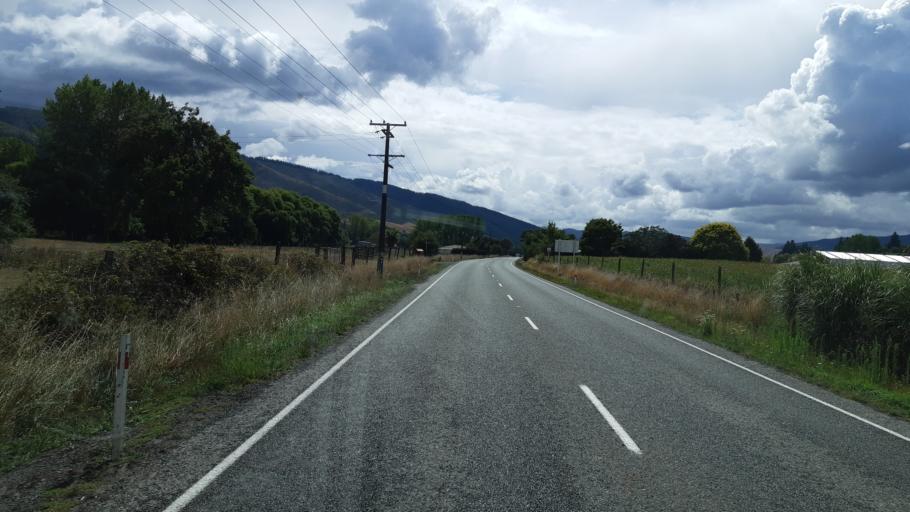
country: NZ
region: Tasman
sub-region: Tasman District
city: Wakefield
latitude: -41.4718
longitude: 172.8063
